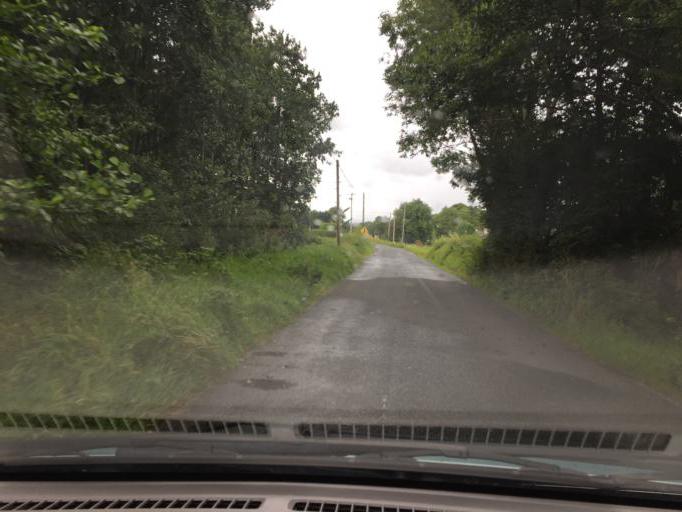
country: IE
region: Connaught
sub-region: Sligo
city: Tobercurry
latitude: 54.0358
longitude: -8.8050
